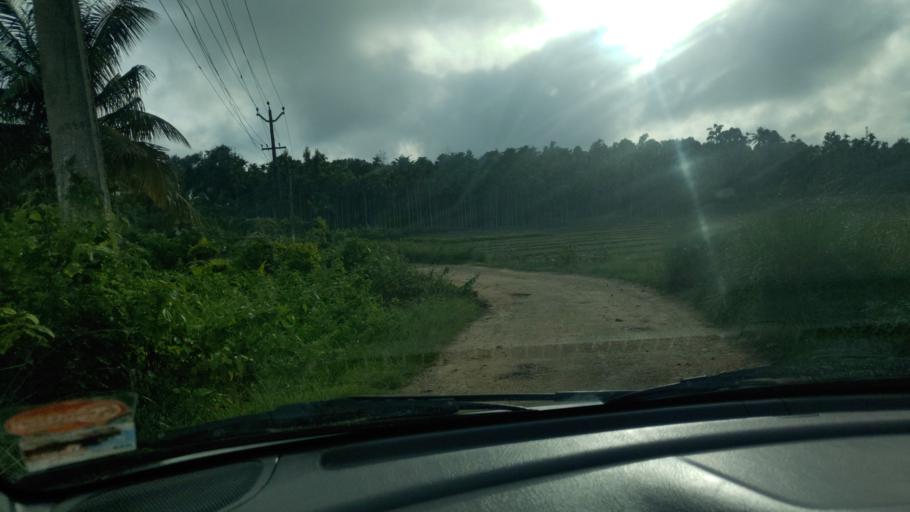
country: IN
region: Kerala
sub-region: Wayanad
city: Panamaram
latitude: 11.7256
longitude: 76.2831
